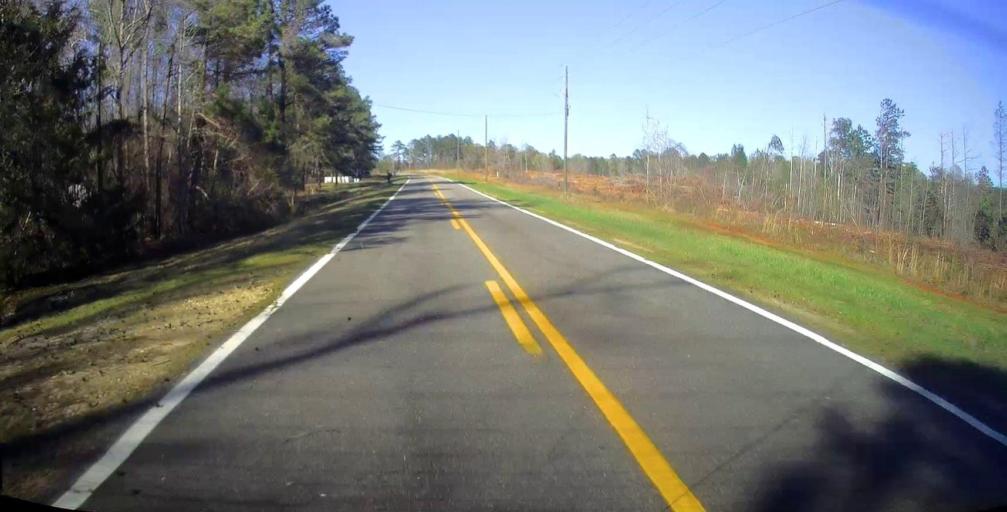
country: US
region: Georgia
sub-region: Taylor County
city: Reynolds
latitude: 32.5815
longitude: -83.9918
